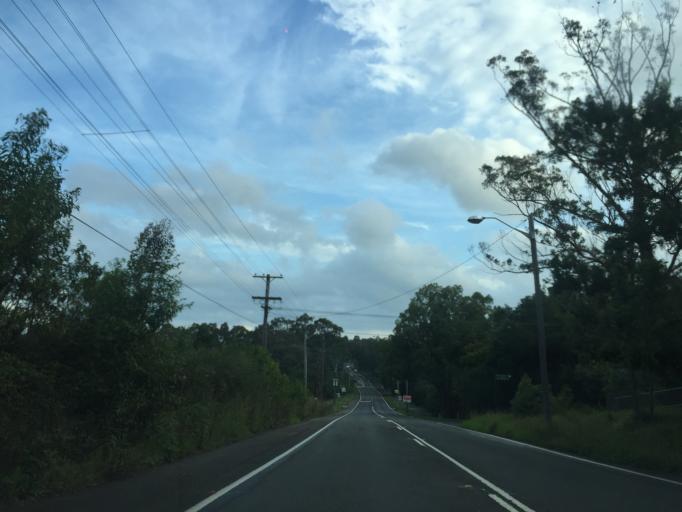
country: AU
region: New South Wales
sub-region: The Hills Shire
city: Glenhaven
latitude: -33.6987
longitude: 151.0159
